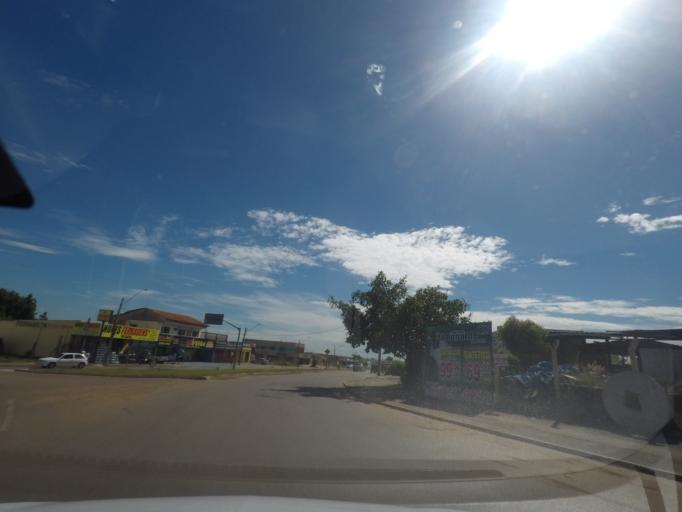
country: BR
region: Goias
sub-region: Aparecida De Goiania
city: Aparecida de Goiania
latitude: -16.7977
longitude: -49.2834
